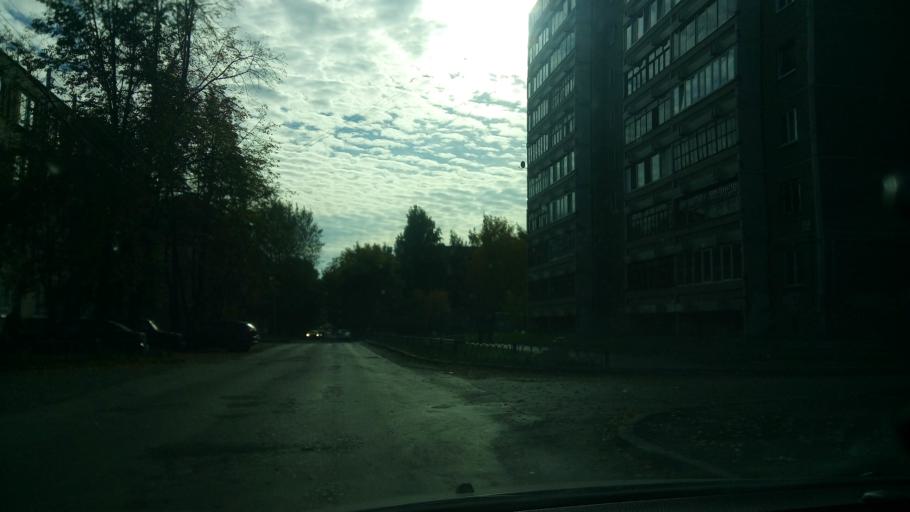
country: RU
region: Sverdlovsk
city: Yekaterinburg
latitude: 56.9023
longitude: 60.6024
